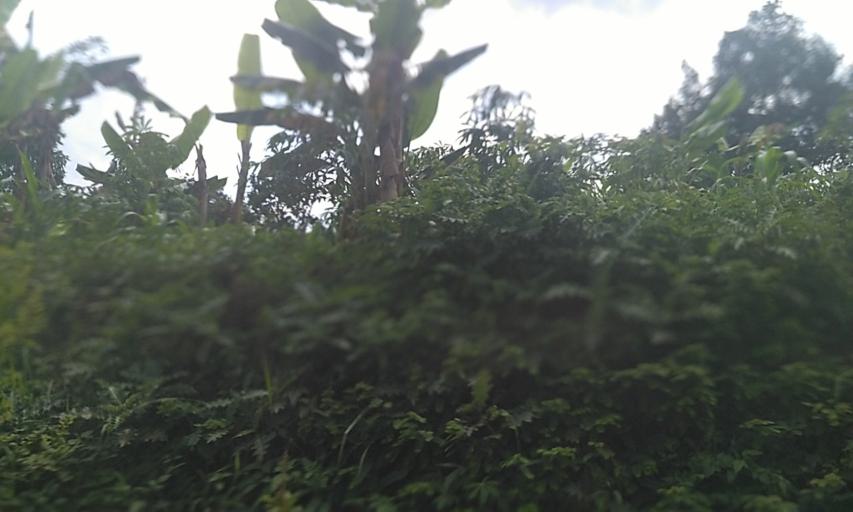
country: UG
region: Central Region
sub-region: Wakiso District
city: Wakiso
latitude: 0.3547
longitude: 32.4630
